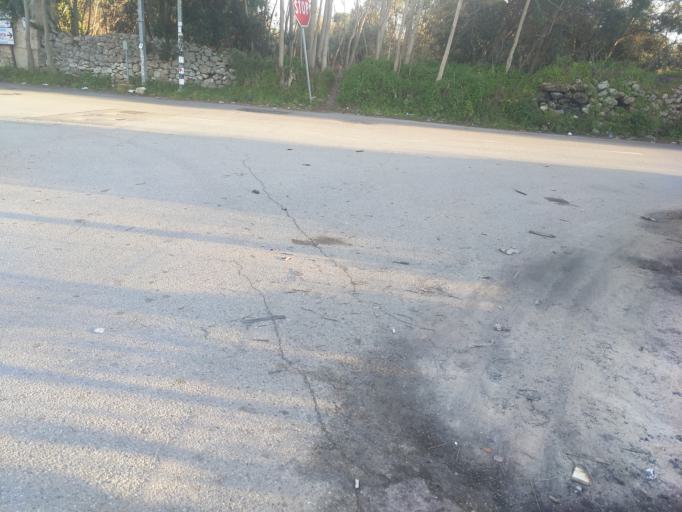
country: IT
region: Apulia
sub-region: Provincia di Bari
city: Bari
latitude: 41.1134
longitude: 16.8440
